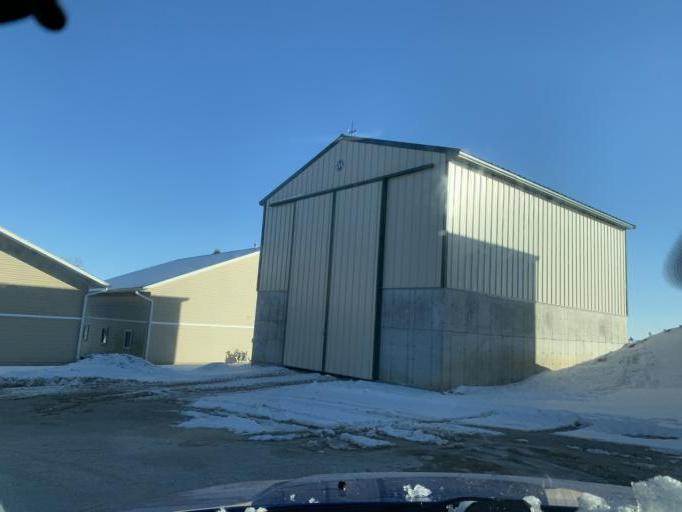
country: US
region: Wisconsin
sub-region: Dane County
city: Cross Plains
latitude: 43.0605
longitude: -89.6594
